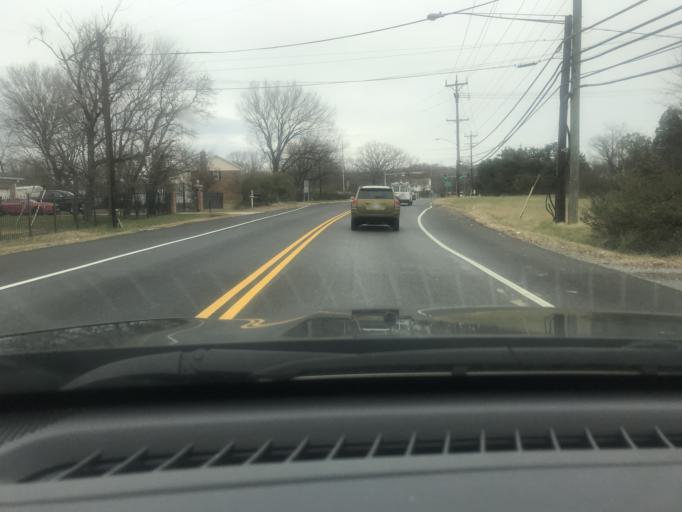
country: US
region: Maryland
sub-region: Prince George's County
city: Friendly
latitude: 38.7748
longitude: -76.9592
